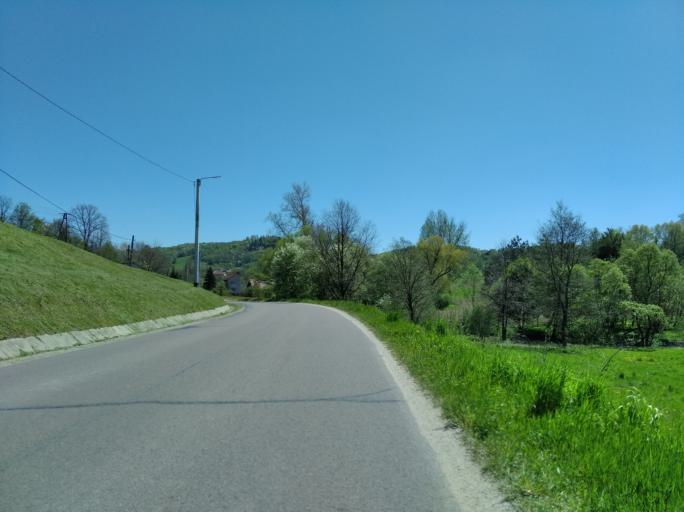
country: PL
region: Subcarpathian Voivodeship
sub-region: Powiat debicki
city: Brzostek
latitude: 49.9174
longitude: 21.4047
